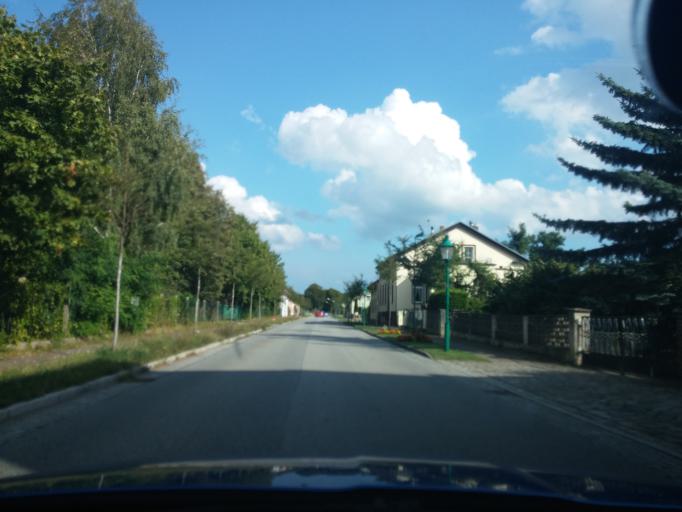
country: DE
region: Brandenburg
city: Halbe
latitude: 52.1086
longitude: 13.7681
